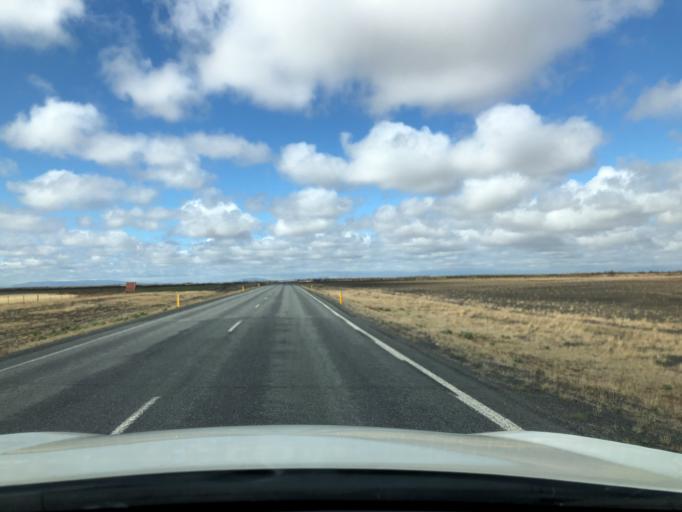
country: IS
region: South
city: Vestmannaeyjar
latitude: 63.8019
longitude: -20.3238
